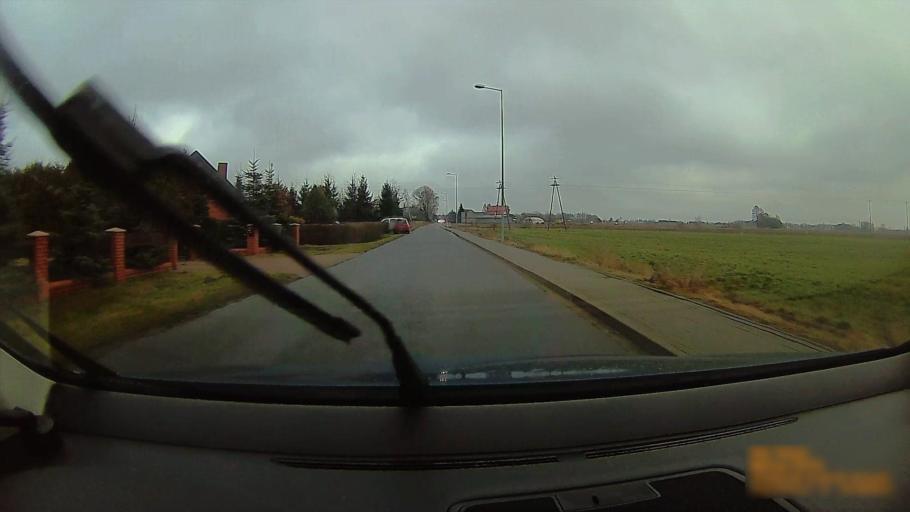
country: PL
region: Greater Poland Voivodeship
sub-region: Powiat koninski
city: Rychwal
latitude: 52.0754
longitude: 18.1493
